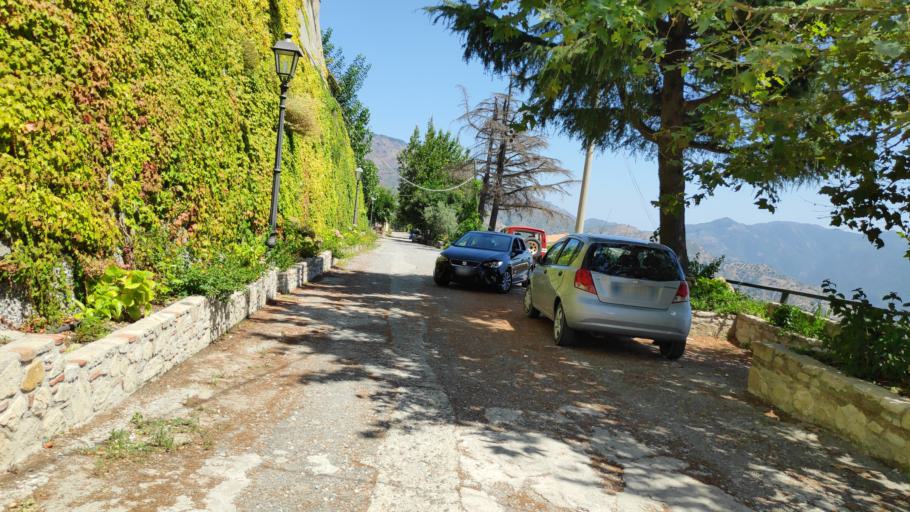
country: IT
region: Calabria
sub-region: Provincia di Reggio Calabria
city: Bova
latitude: 37.9946
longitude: 15.9339
